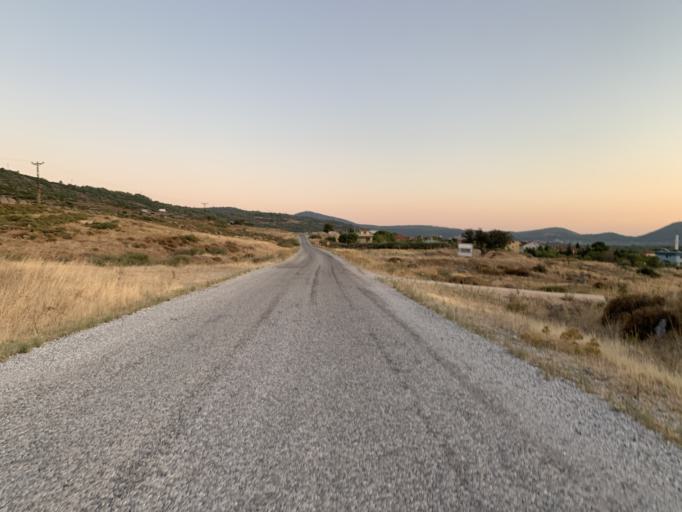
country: TR
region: Izmir
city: Uzunkuyu
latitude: 38.3274
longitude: 26.5836
